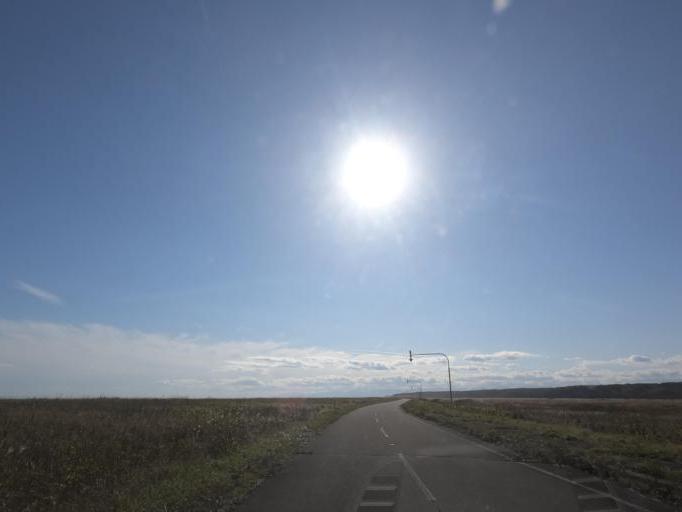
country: JP
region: Hokkaido
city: Obihiro
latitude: 42.5945
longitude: 143.5445
